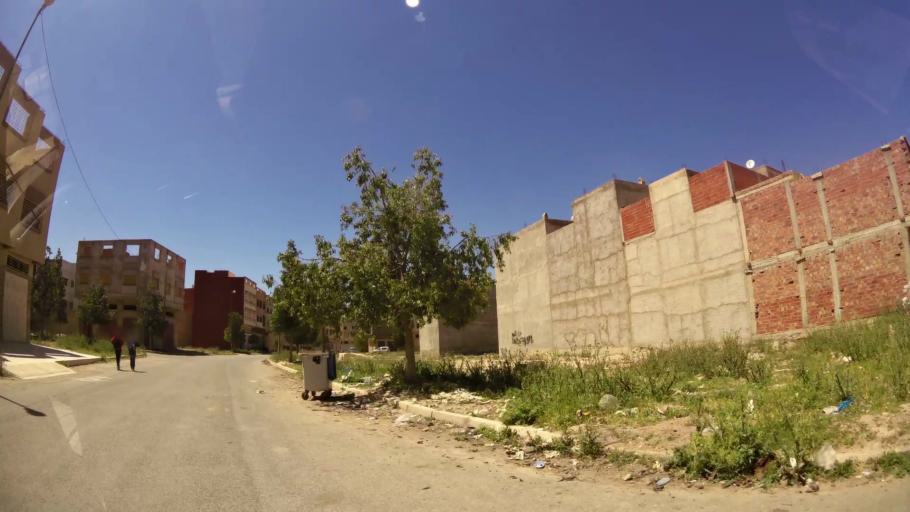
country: MA
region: Oriental
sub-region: Oujda-Angad
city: Oujda
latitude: 34.6807
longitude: -1.8647
